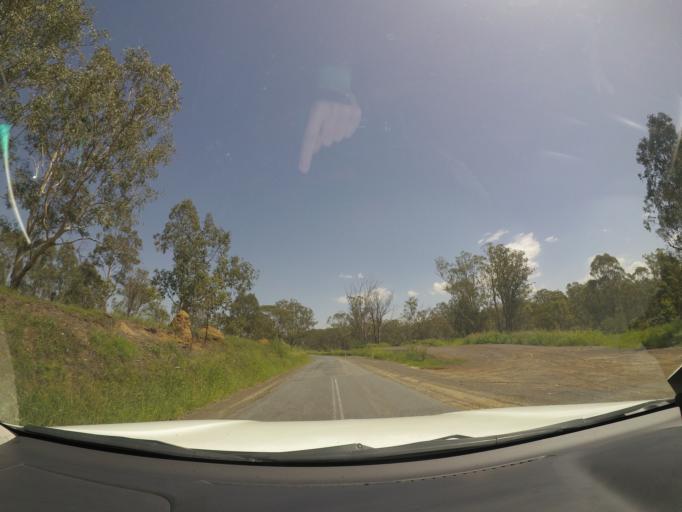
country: AU
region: Queensland
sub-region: Logan
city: Cedar Vale
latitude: -27.8650
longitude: 152.9299
